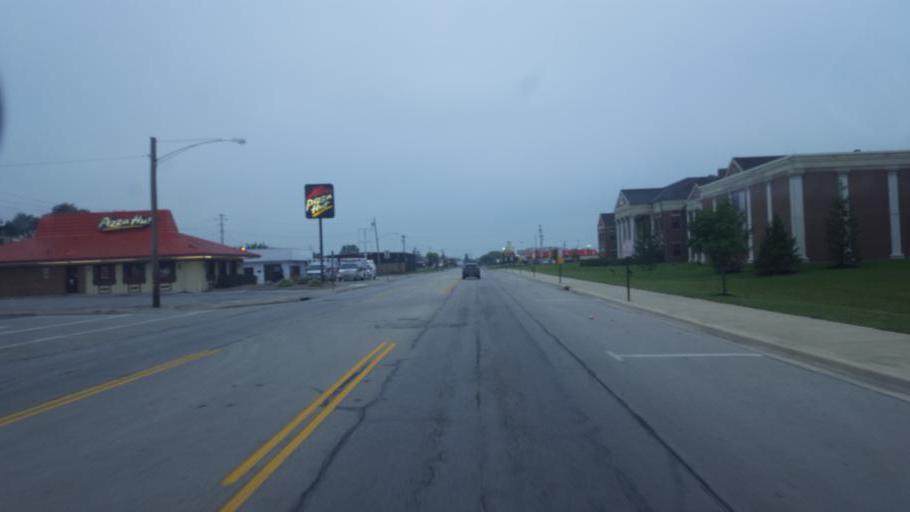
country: US
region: Ohio
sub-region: Fayette County
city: Washington Court House
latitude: 39.5426
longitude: -83.4263
